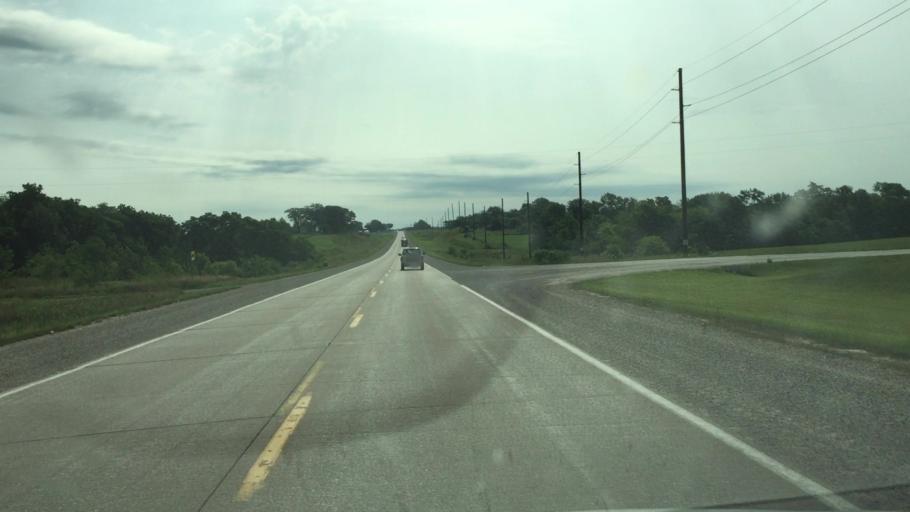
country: US
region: Illinois
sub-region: Hancock County
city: Nauvoo
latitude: 40.6390
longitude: -91.5471
